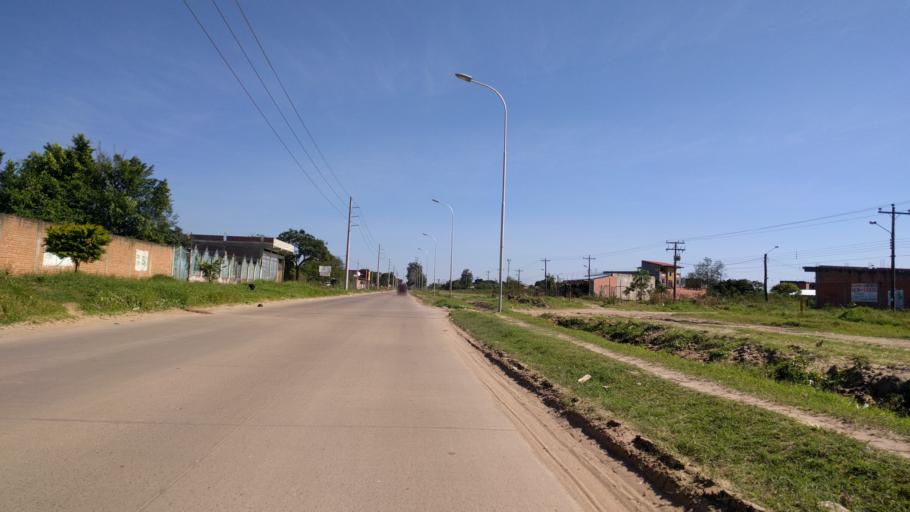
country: BO
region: Santa Cruz
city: Santa Cruz de la Sierra
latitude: -17.8701
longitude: -63.1967
